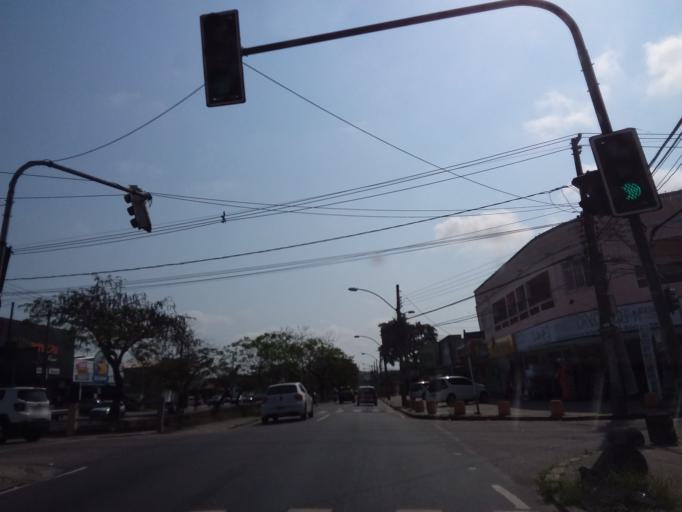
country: BR
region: Rio de Janeiro
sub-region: Nilopolis
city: Nilopolis
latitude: -22.9017
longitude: -43.5461
